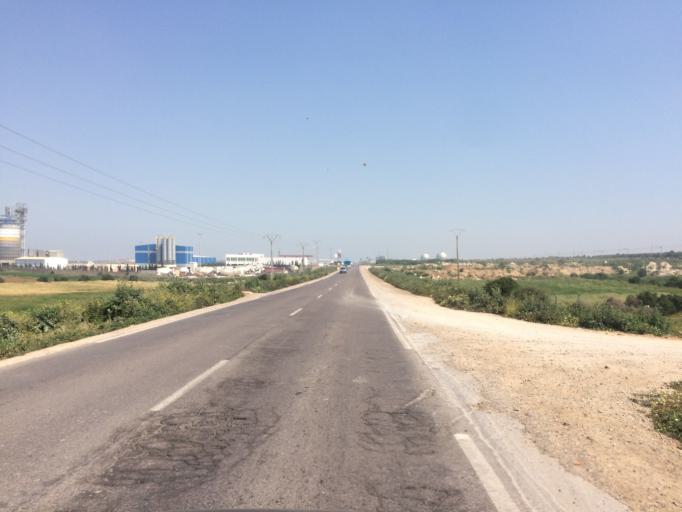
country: MA
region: Doukkala-Abda
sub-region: El-Jadida
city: Moulay Abdallah
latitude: 33.1547
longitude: -8.6045
